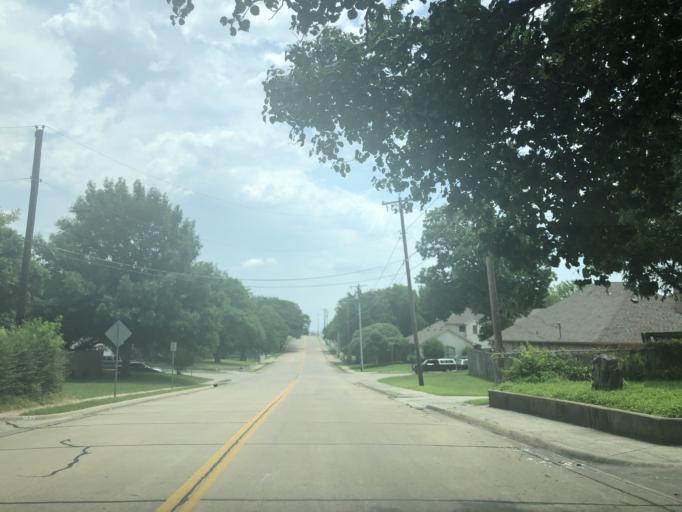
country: US
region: Texas
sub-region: Dallas County
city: Irving
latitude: 32.7975
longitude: -96.9291
